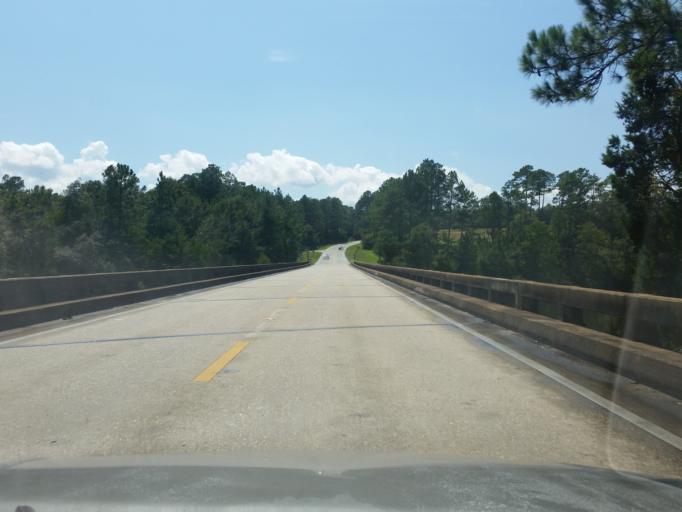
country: US
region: Florida
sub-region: Escambia County
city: Cantonment
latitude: 30.5189
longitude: -87.4624
